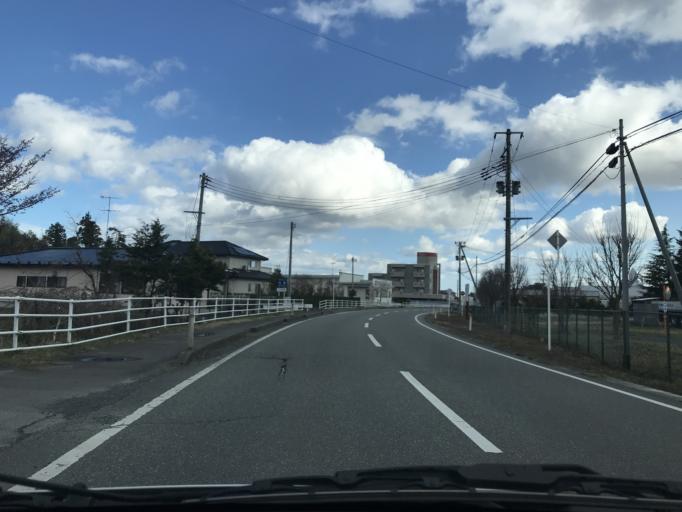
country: JP
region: Miyagi
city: Wakuya
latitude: 38.6711
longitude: 141.1937
